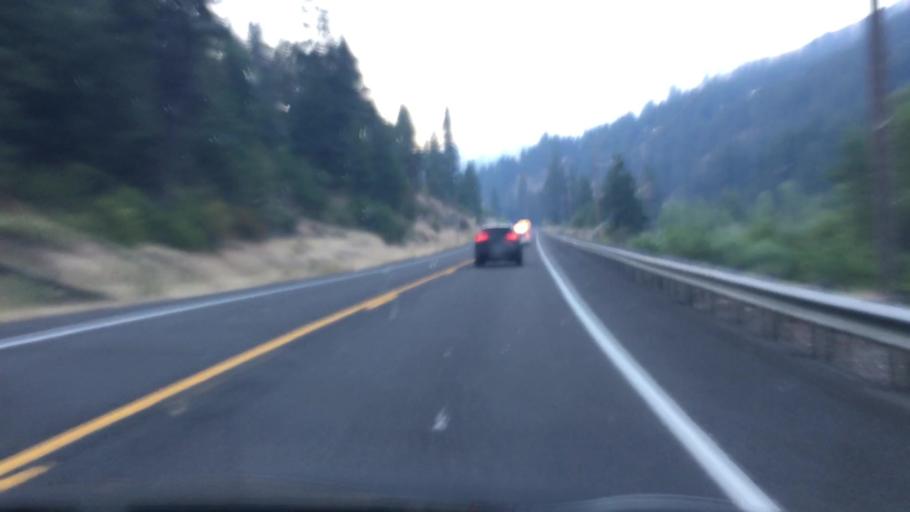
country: US
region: Idaho
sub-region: Valley County
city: McCall
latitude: 45.2061
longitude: -116.3130
